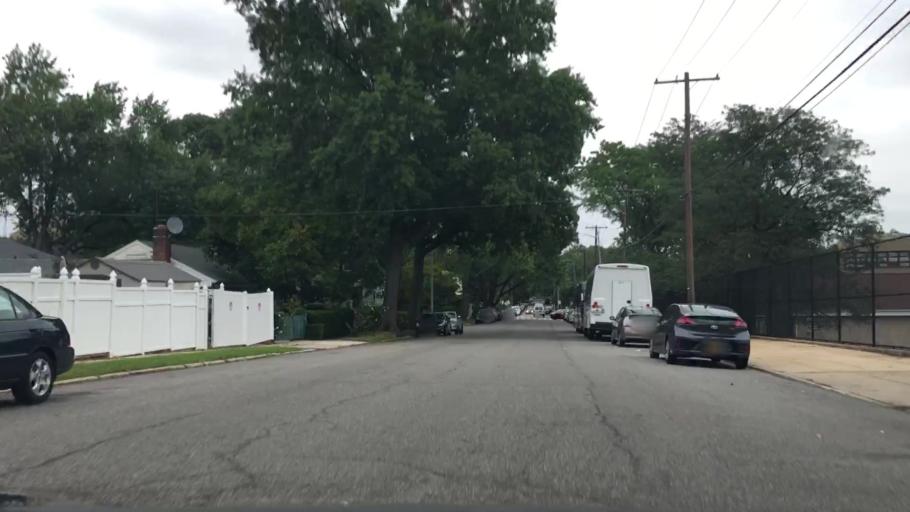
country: US
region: New York
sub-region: Nassau County
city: Bellerose Terrace
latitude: 40.7349
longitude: -73.7404
